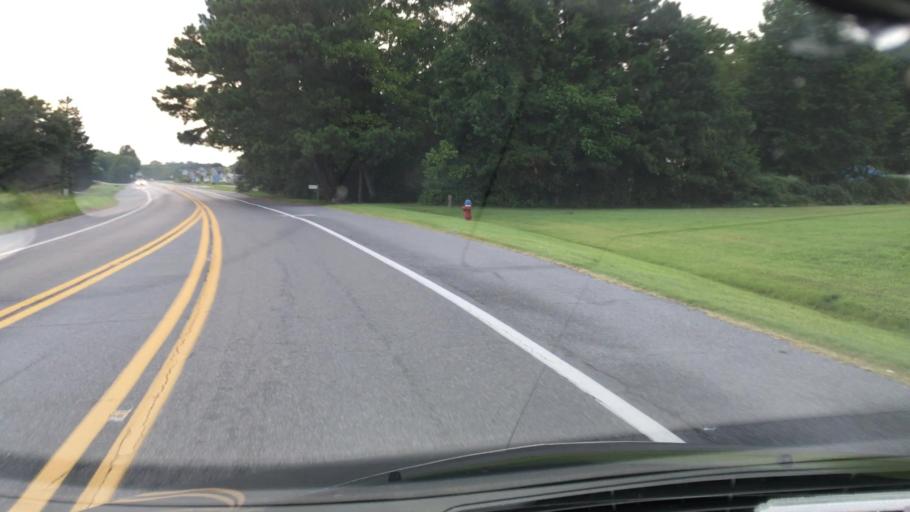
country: US
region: Delaware
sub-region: Sussex County
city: Bethany Beach
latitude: 38.5251
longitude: -75.0740
